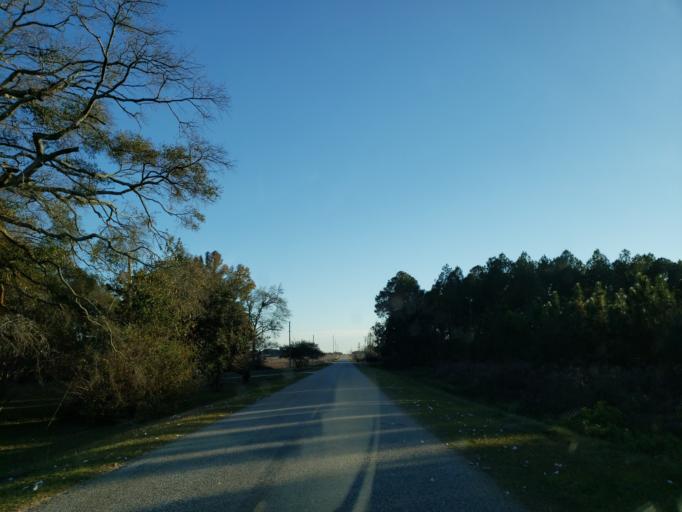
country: US
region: Georgia
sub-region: Dooly County
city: Vienna
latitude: 32.1509
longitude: -83.7609
